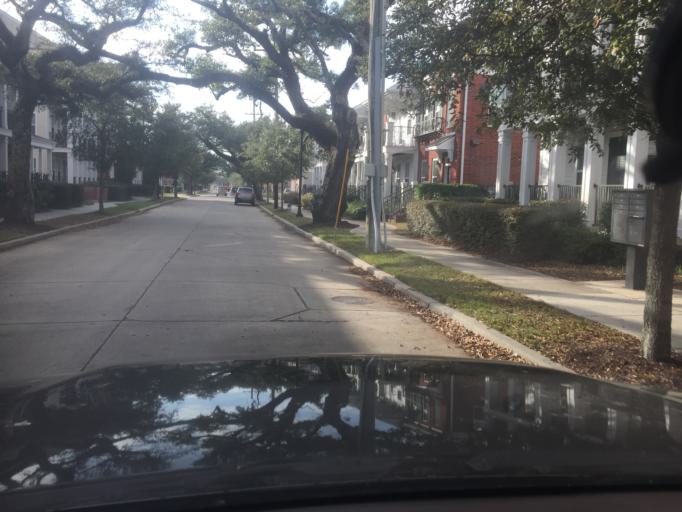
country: US
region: Louisiana
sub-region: Orleans Parish
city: New Orleans
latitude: 29.9962
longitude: -90.0758
